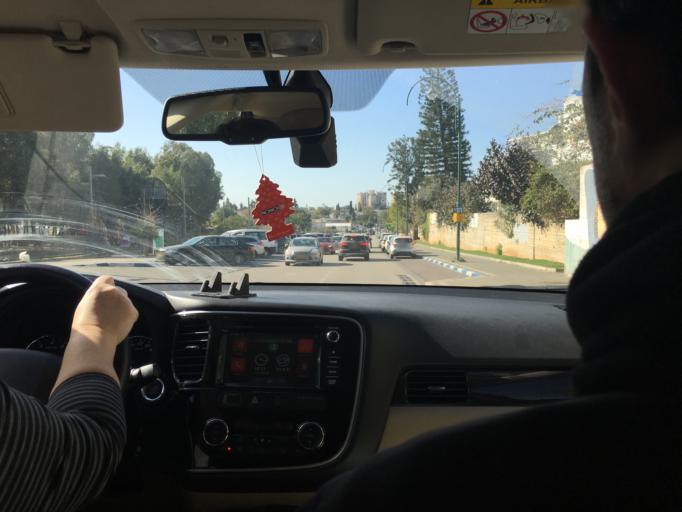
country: IL
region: Tel Aviv
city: Ramat HaSharon
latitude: 32.1398
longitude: 34.8457
